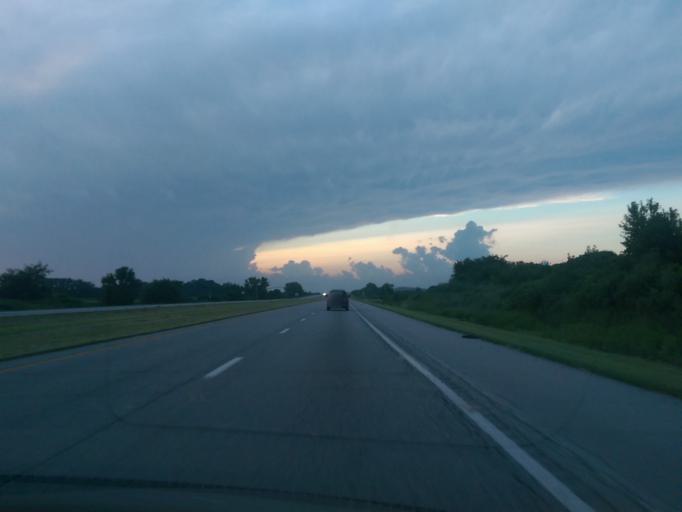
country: US
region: Iowa
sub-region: Fremont County
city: Hamburg
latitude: 40.5609
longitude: -95.6357
